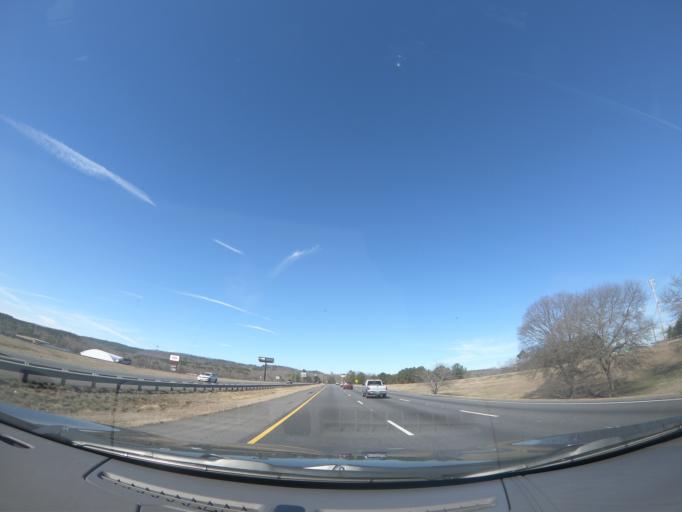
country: US
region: Georgia
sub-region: Catoosa County
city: Ringgold
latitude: 34.8931
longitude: -85.0755
